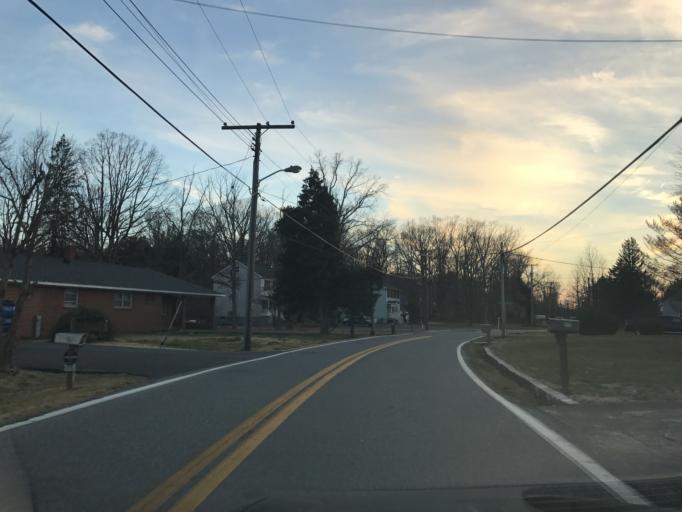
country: US
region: Maryland
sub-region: Baltimore County
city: Middle River
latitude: 39.2991
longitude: -76.4241
